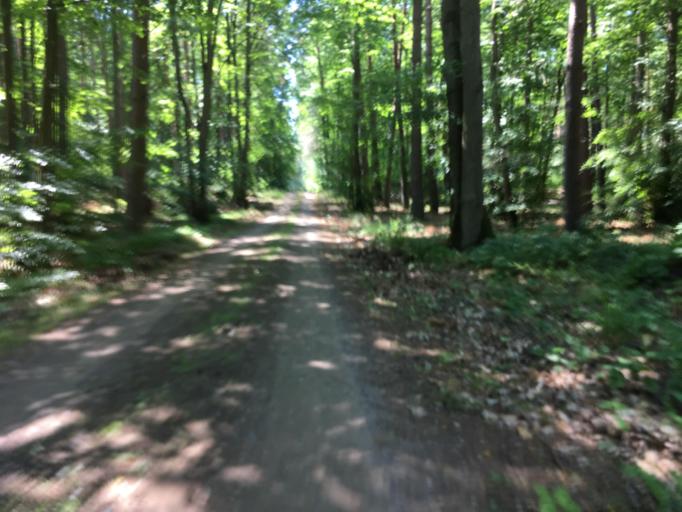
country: DE
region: Brandenburg
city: Marienwerder
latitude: 52.9202
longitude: 13.6473
